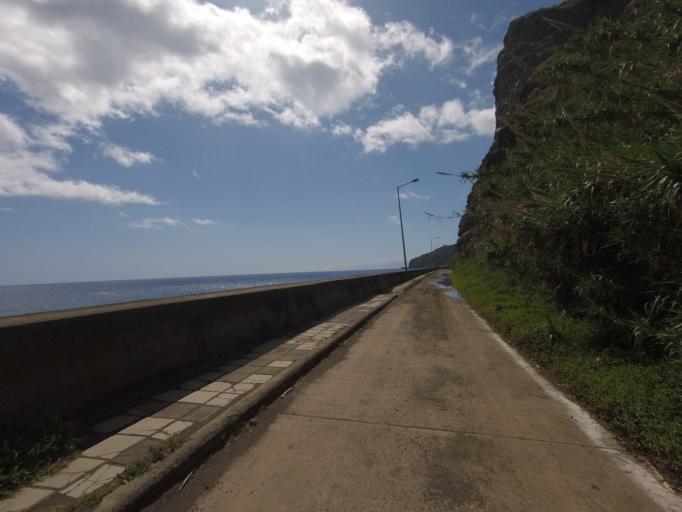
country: PT
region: Madeira
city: Ponta do Sol
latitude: 32.6760
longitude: -17.0746
